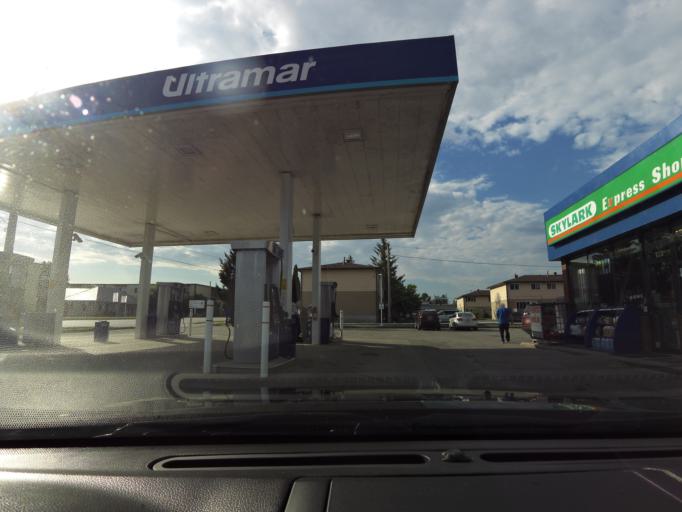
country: CA
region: Ontario
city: Orillia
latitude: 44.6245
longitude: -79.4336
